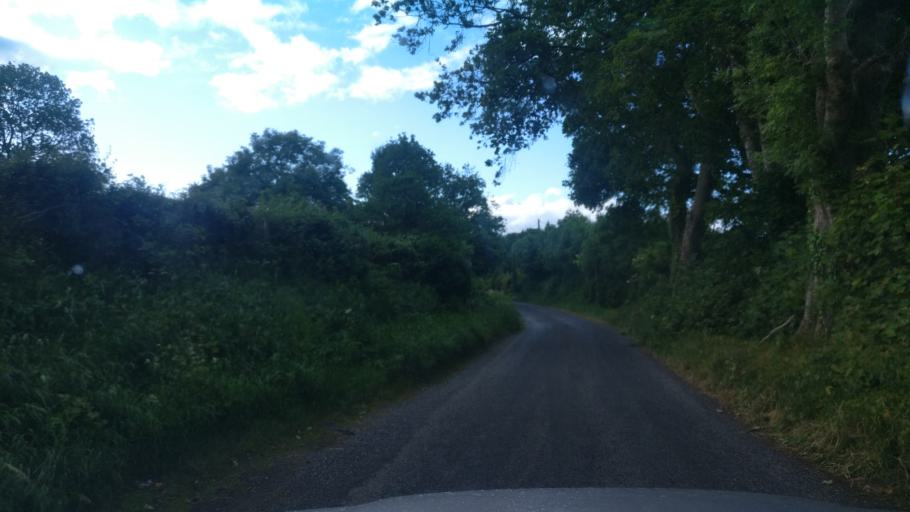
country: IE
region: Connaught
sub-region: County Galway
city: Ballinasloe
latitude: 53.2437
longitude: -8.2293
